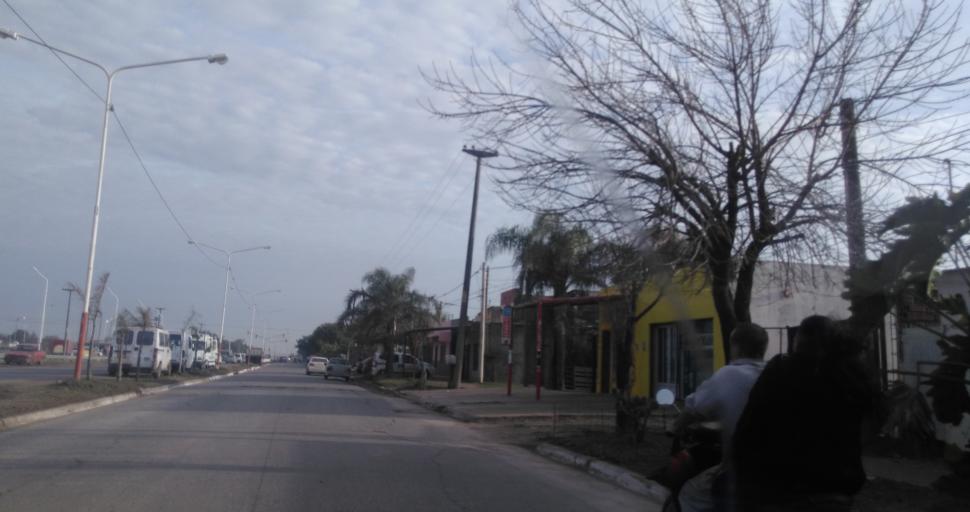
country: AR
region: Chaco
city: Resistencia
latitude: -27.4717
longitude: -59.0064
